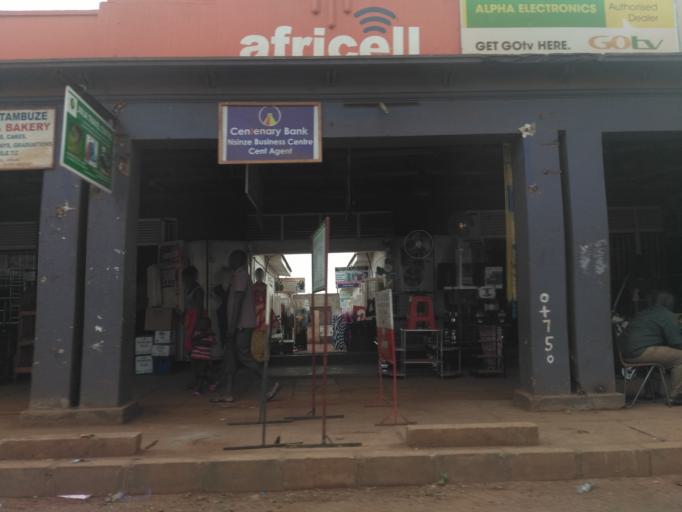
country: UG
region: Eastern Region
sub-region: Jinja District
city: Jinja
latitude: 0.4297
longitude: 33.2100
